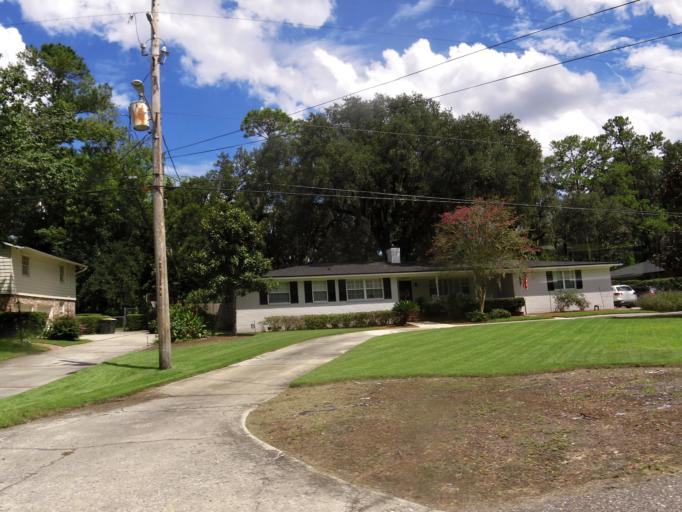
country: US
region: Florida
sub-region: Duval County
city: Jacksonville
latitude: 30.2671
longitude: -81.7141
